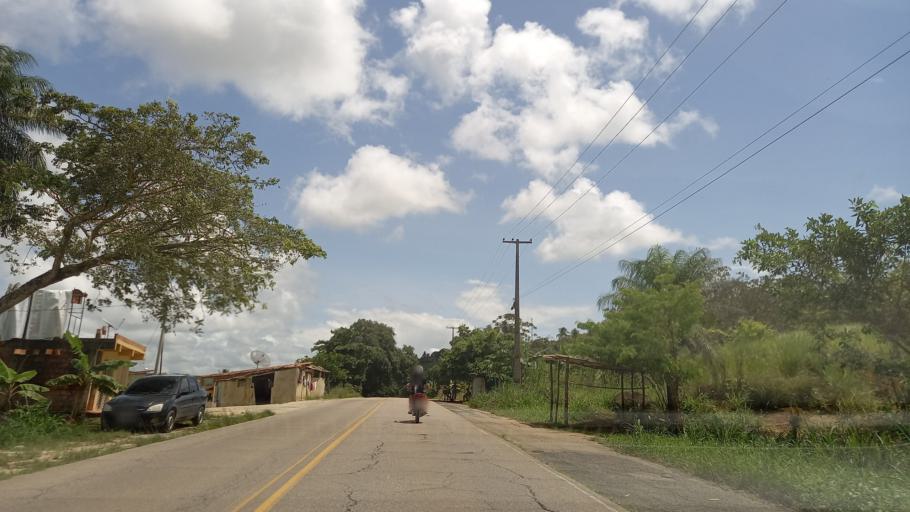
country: BR
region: Pernambuco
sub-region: Rio Formoso
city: Rio Formoso
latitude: -8.6558
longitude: -35.1484
